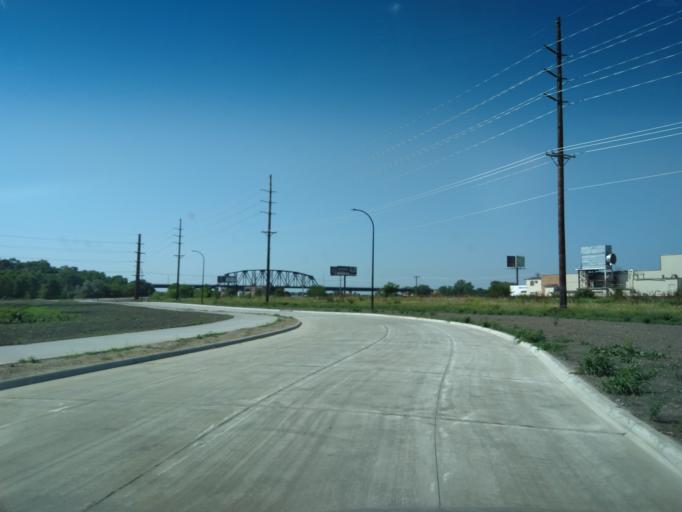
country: US
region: Iowa
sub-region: Woodbury County
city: Sioux City
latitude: 42.4804
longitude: -96.3854
